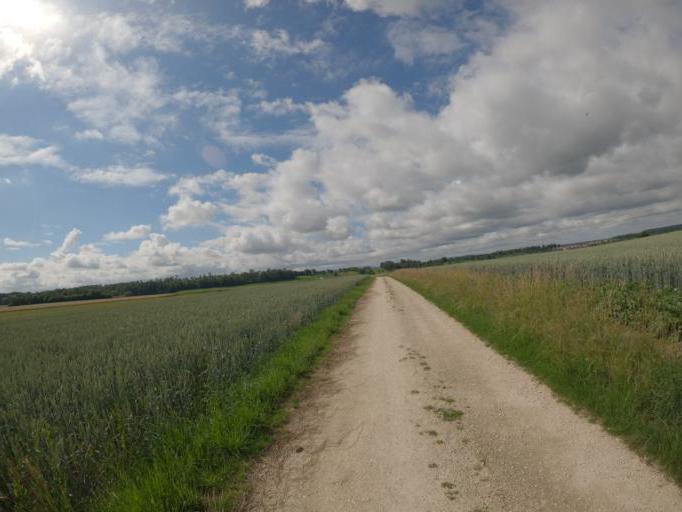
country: DE
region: Baden-Wuerttemberg
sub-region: Regierungsbezirk Stuttgart
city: Ebersbach an der Fils
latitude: 48.6978
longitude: 9.5168
